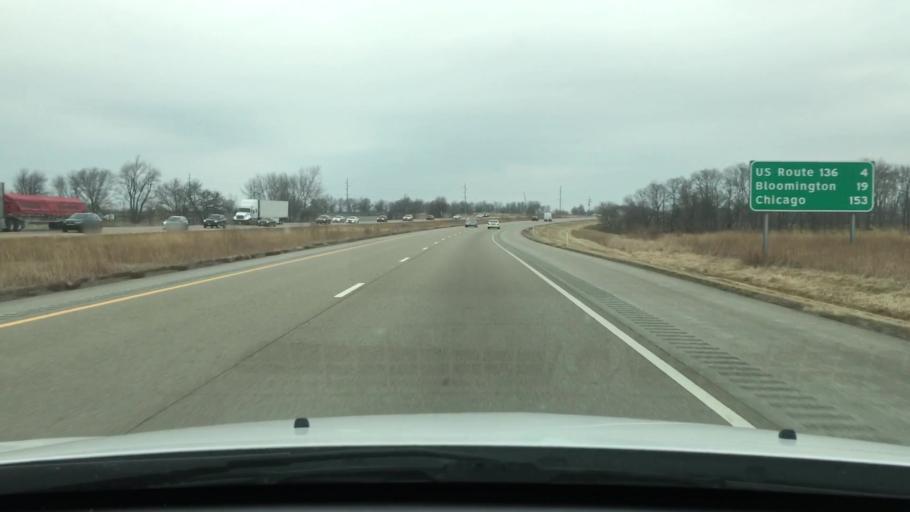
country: US
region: Illinois
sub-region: Logan County
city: Atlanta
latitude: 40.2724
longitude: -89.2127
